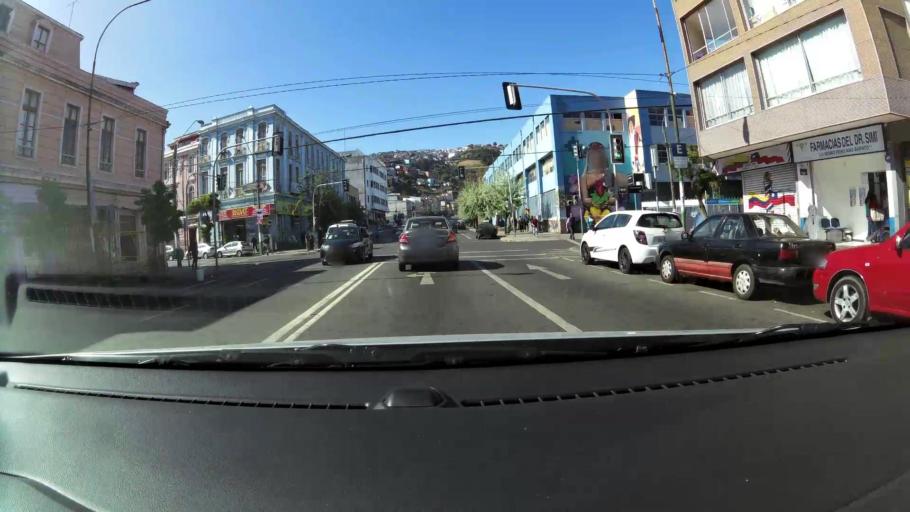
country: CL
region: Valparaiso
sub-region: Provincia de Valparaiso
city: Valparaiso
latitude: -33.0486
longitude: -71.6129
